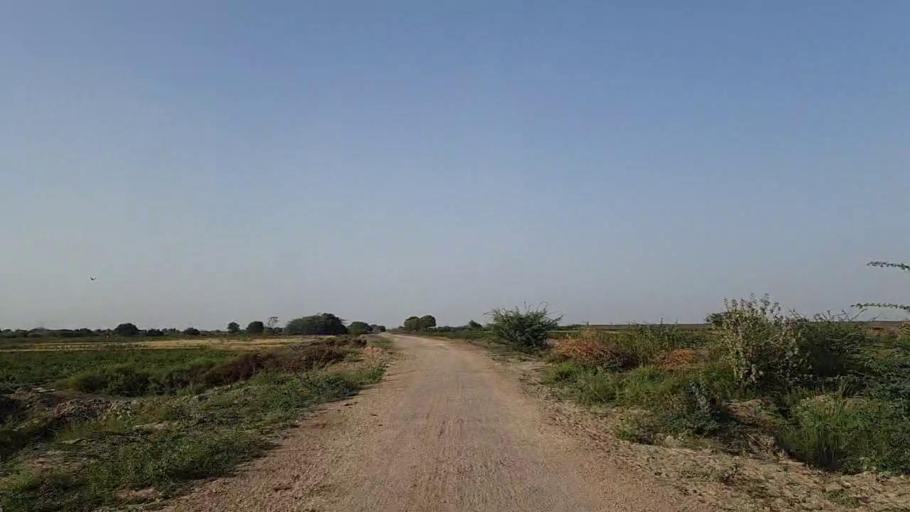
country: PK
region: Sindh
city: Jati
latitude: 24.3137
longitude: 68.1690
